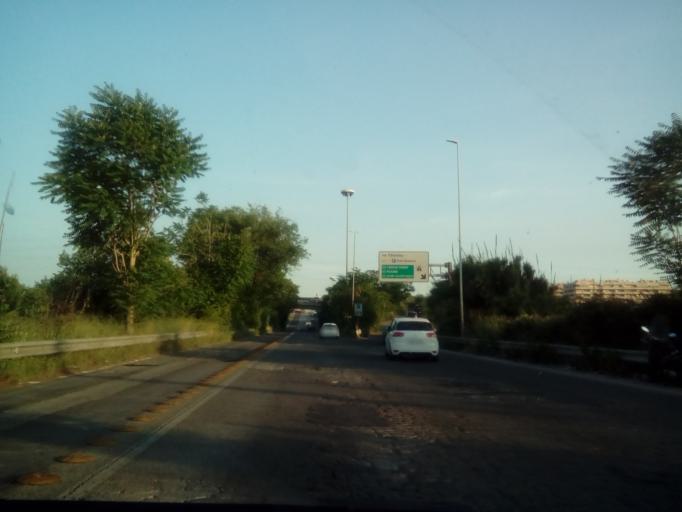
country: IT
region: Latium
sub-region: Citta metropolitana di Roma Capitale
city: Rome
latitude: 41.9067
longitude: 12.5731
